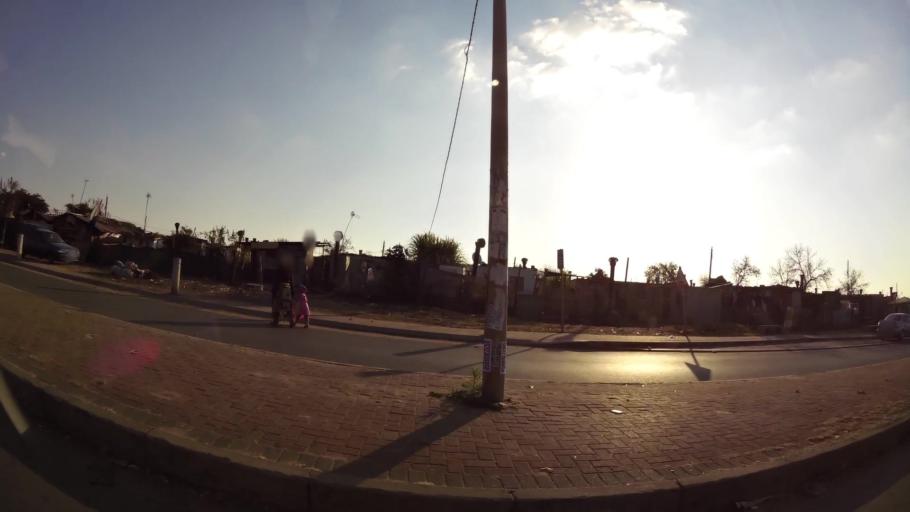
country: ZA
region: Gauteng
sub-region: Ekurhuleni Metropolitan Municipality
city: Tembisa
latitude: -26.0061
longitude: 28.1900
